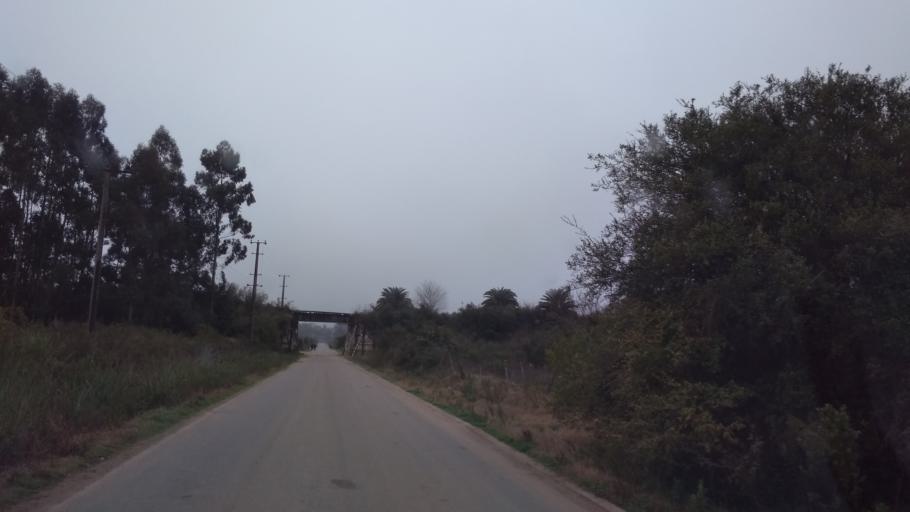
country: UY
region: Florida
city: Florida
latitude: -34.0874
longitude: -56.2074
